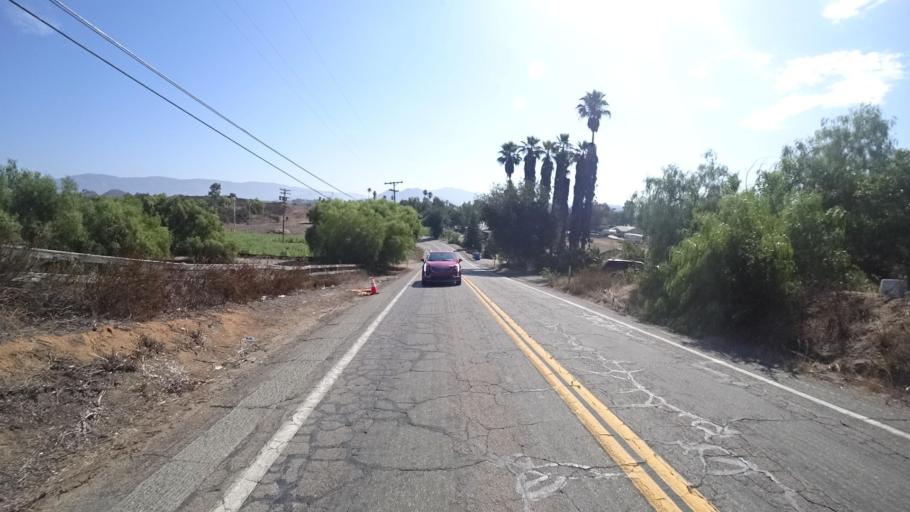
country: US
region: California
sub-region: San Diego County
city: Valley Center
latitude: 33.2316
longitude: -117.0166
